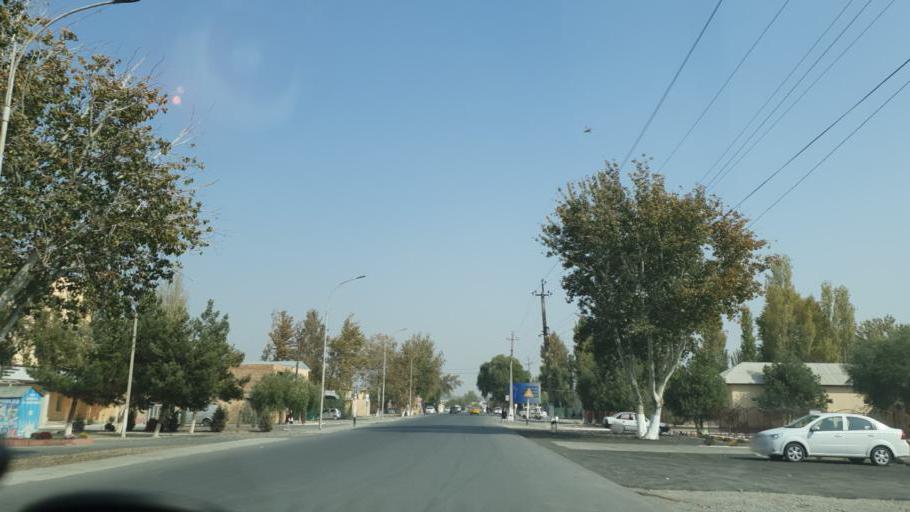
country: UZ
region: Fergana
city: Beshariq
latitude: 40.4347
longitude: 70.5927
